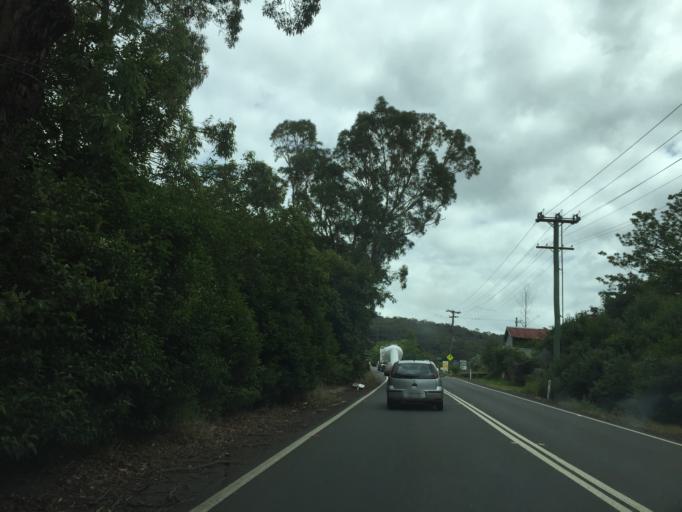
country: AU
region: New South Wales
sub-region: Hawkesbury
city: Richmond
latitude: -33.5433
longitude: 150.6460
